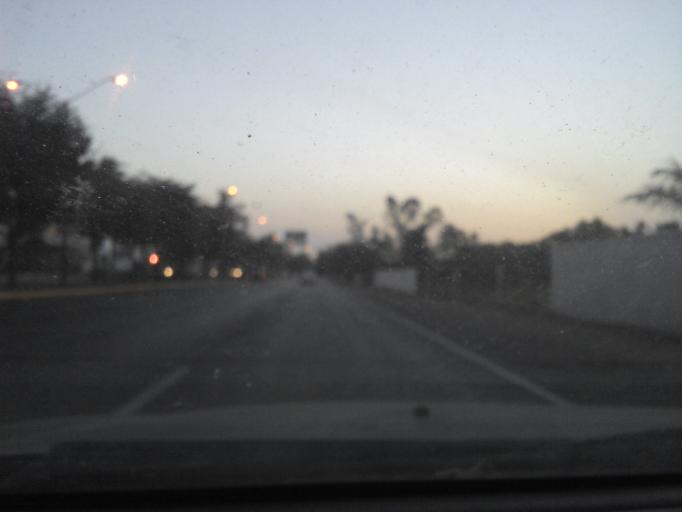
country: MX
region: Sinaloa
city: Culiacan
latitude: 24.7912
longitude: -107.4388
